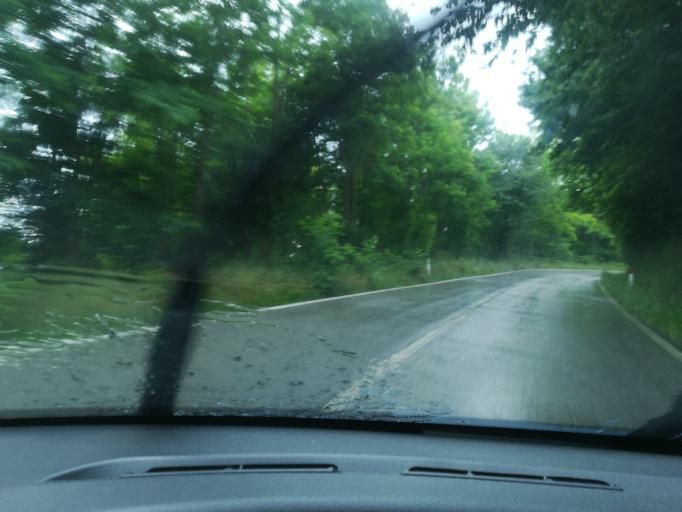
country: IT
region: The Marches
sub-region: Province of Fermo
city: Amandola
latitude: 42.9997
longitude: 13.3390
